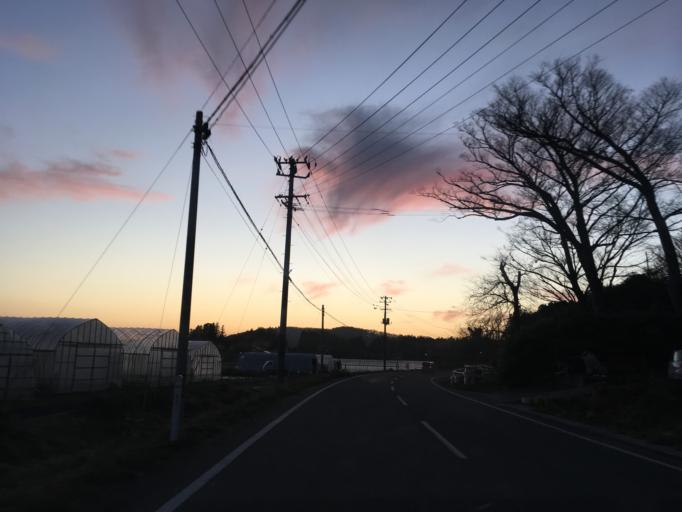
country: JP
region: Iwate
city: Ichinoseki
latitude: 38.7440
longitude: 141.2238
